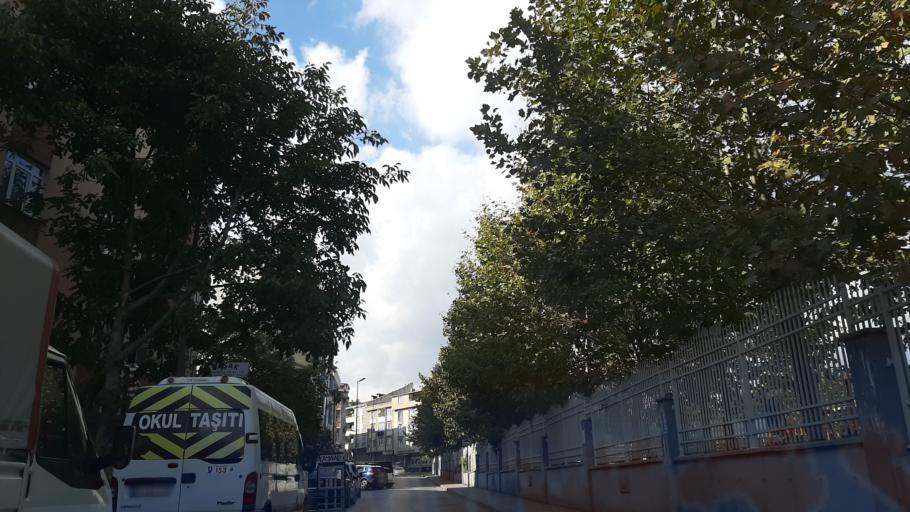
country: TR
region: Istanbul
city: Esenyurt
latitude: 41.0365
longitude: 28.6583
